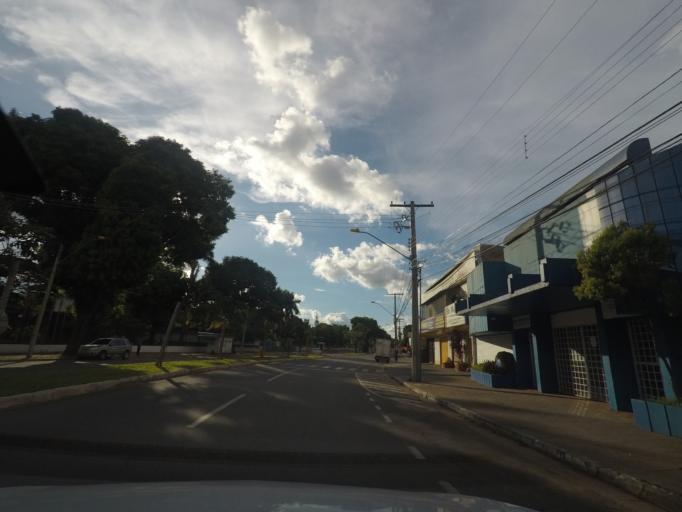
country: BR
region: Goias
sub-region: Goiania
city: Goiania
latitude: -16.6825
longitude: -49.3056
